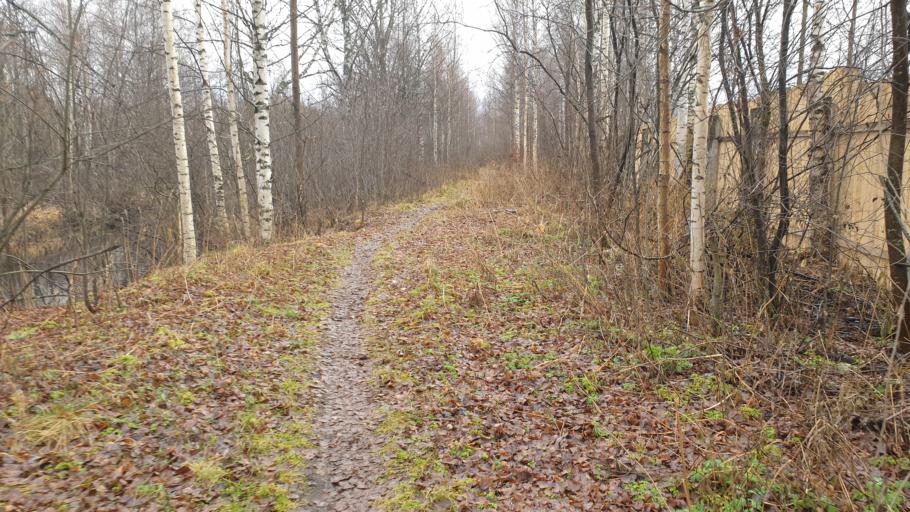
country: RU
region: Kirov
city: Kirs
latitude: 59.3345
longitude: 52.2393
